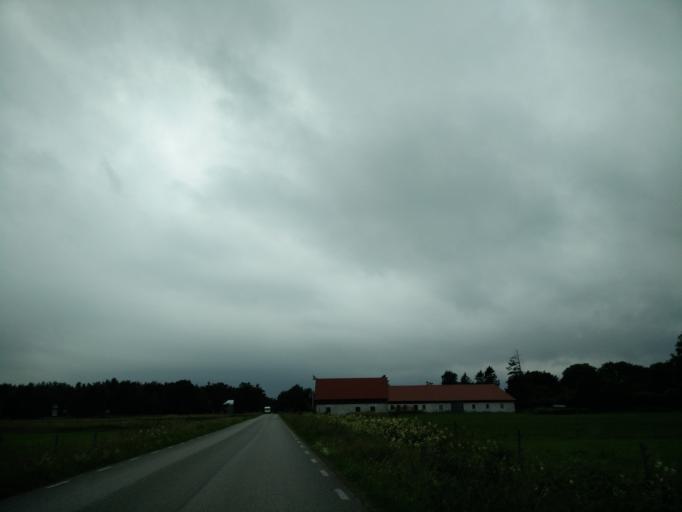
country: SE
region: Gotland
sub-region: Gotland
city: Slite
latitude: 57.9722
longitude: 19.2404
